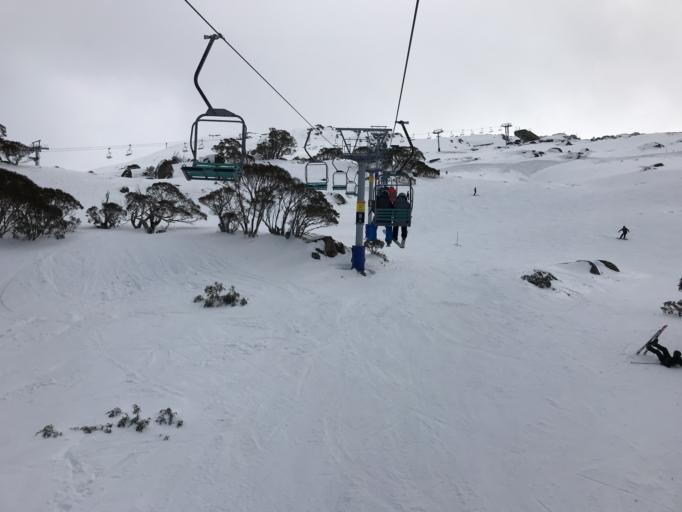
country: AU
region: New South Wales
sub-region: Snowy River
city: Jindabyne
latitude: -36.4005
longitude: 148.3977
